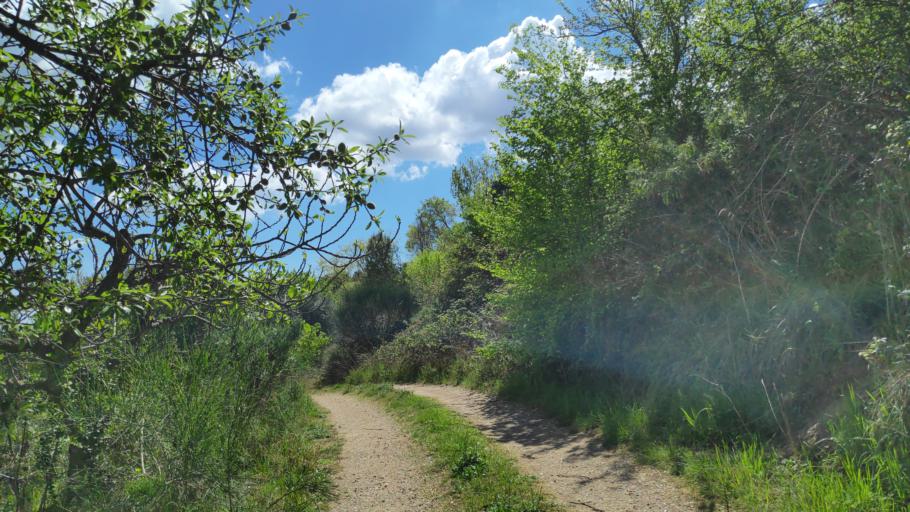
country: ES
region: Catalonia
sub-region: Provincia de Barcelona
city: Polinya
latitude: 41.5452
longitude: 2.1330
